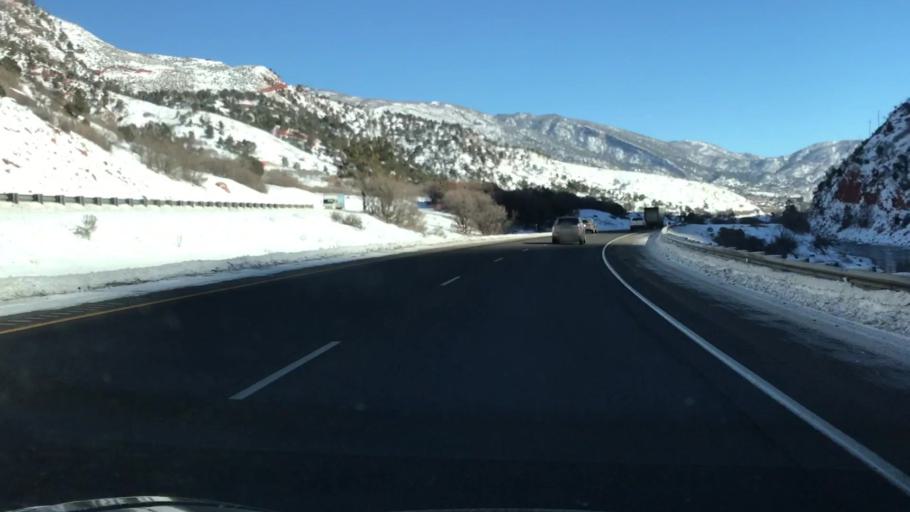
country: US
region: Colorado
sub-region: Garfield County
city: Glenwood Springs
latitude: 39.5595
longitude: -107.3908
